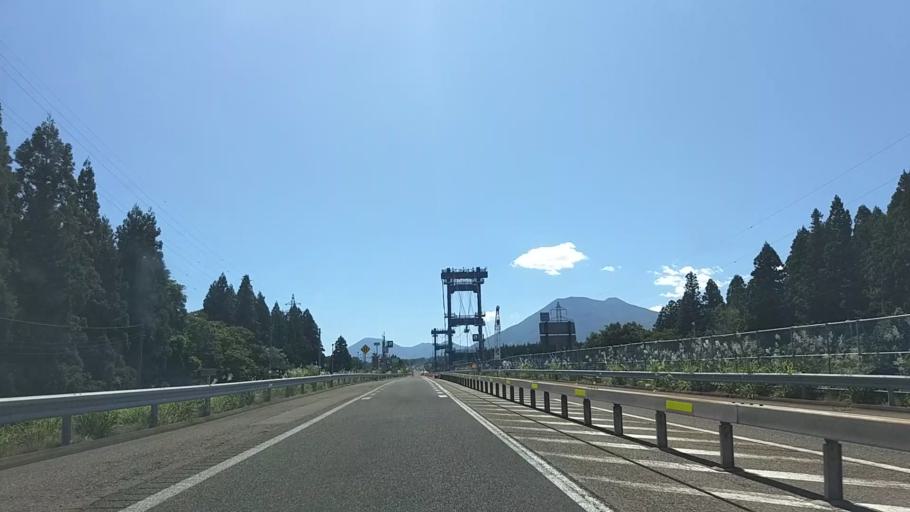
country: JP
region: Niigata
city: Arai
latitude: 36.9100
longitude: 138.2135
